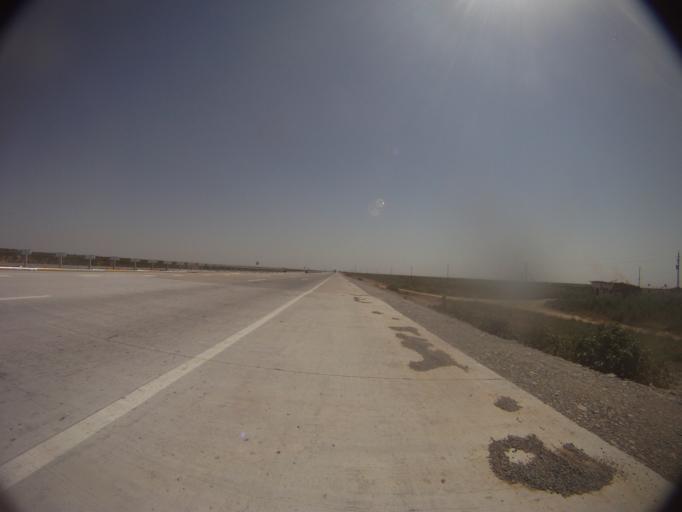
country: KZ
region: Ongtustik Qazaqstan
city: Bayaldyr
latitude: 43.0507
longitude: 68.7003
